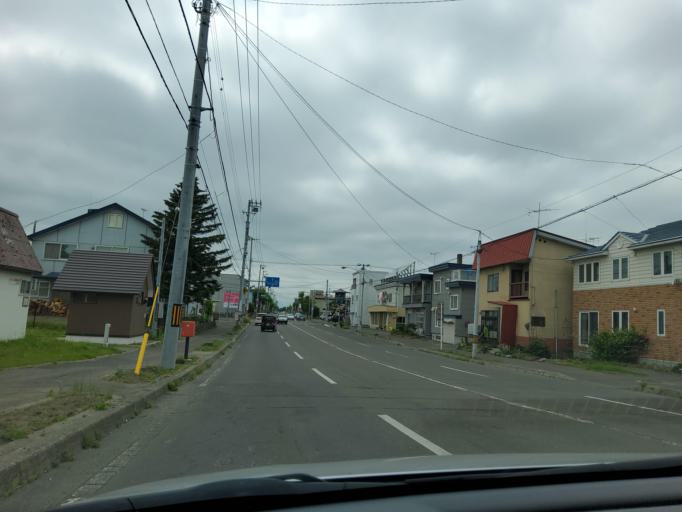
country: JP
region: Hokkaido
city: Obihiro
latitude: 42.9151
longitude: 143.1804
